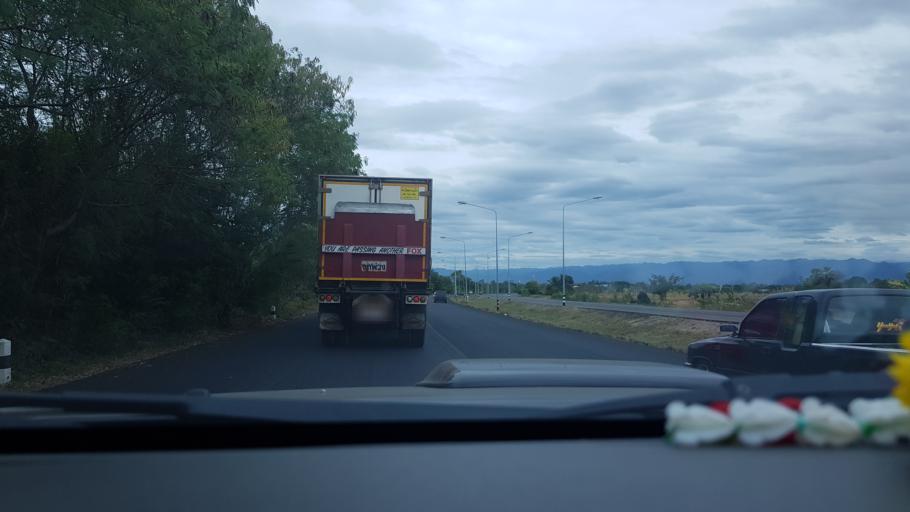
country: TH
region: Phetchabun
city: Phetchabun
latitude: 16.4941
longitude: 101.1448
